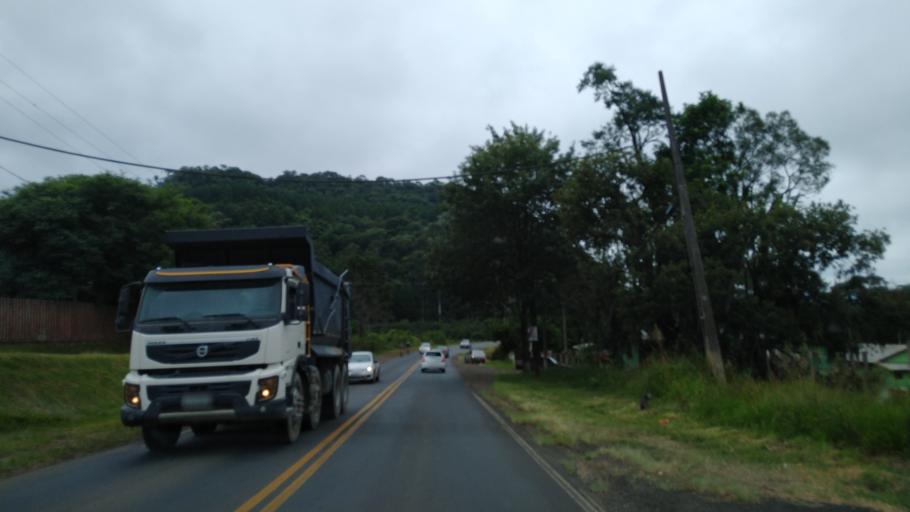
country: BR
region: Parana
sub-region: Uniao Da Vitoria
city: Uniao da Vitoria
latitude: -26.2315
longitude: -51.1271
